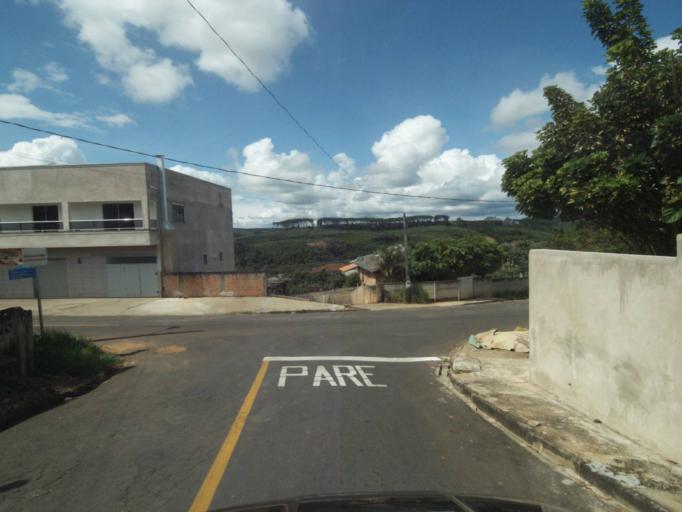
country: BR
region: Parana
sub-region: Telemaco Borba
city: Telemaco Borba
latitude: -24.3154
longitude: -50.6291
